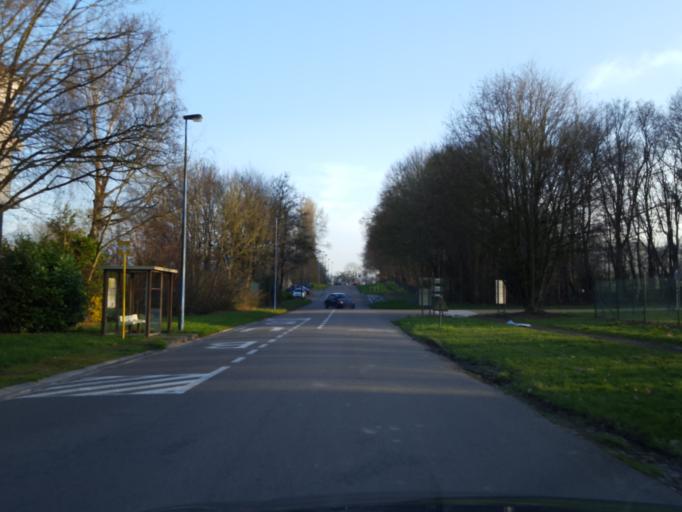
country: BE
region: Wallonia
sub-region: Province du Brabant Wallon
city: Louvain-la-Neuve
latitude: 50.6619
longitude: 4.6410
